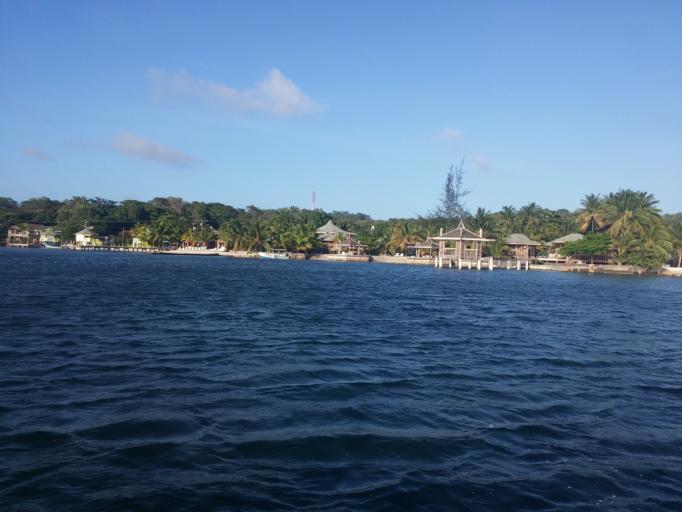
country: HN
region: Bay Islands
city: Sandy Bay
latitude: 16.2998
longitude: -86.5960
